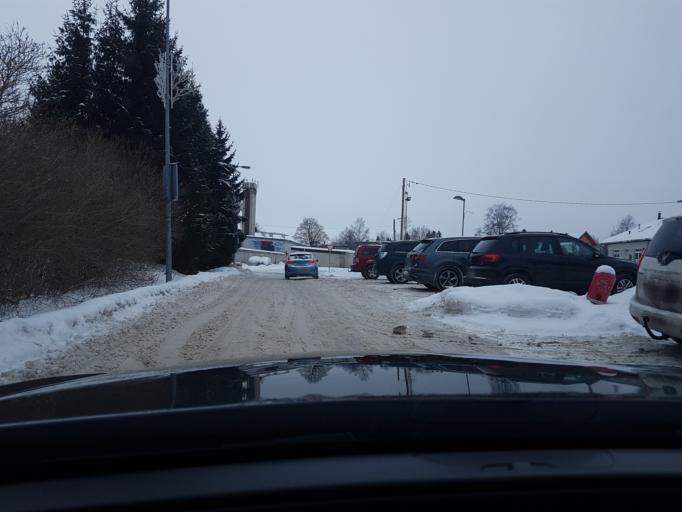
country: EE
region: Harju
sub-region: Saue vald
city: Laagri
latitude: 59.3520
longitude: 24.6369
